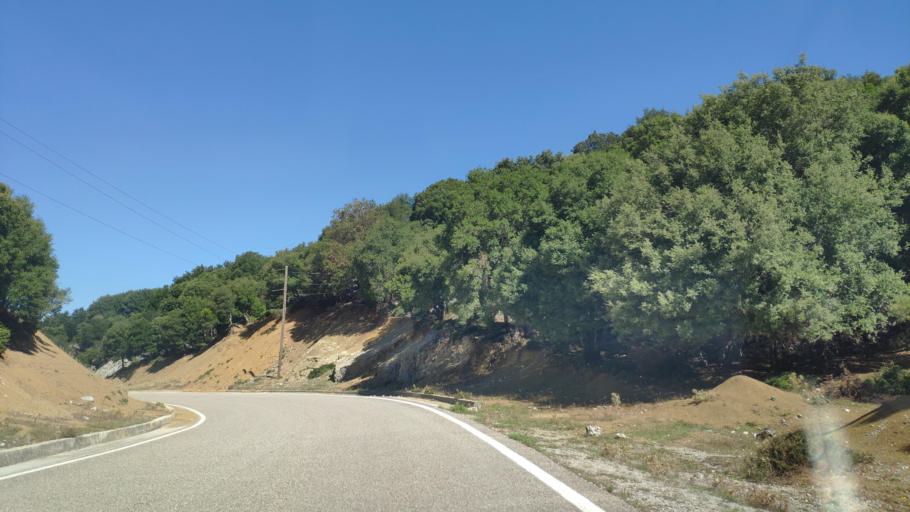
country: GR
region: Central Greece
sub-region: Nomos Evrytanias
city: Kerasochori
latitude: 38.9641
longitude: 21.4620
